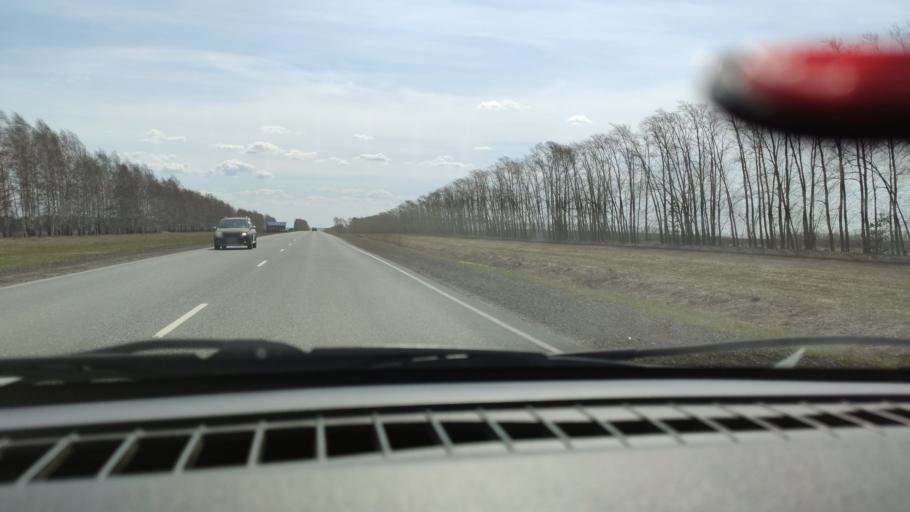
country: RU
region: Bashkortostan
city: Kushnarenkovo
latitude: 55.2273
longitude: 55.0878
